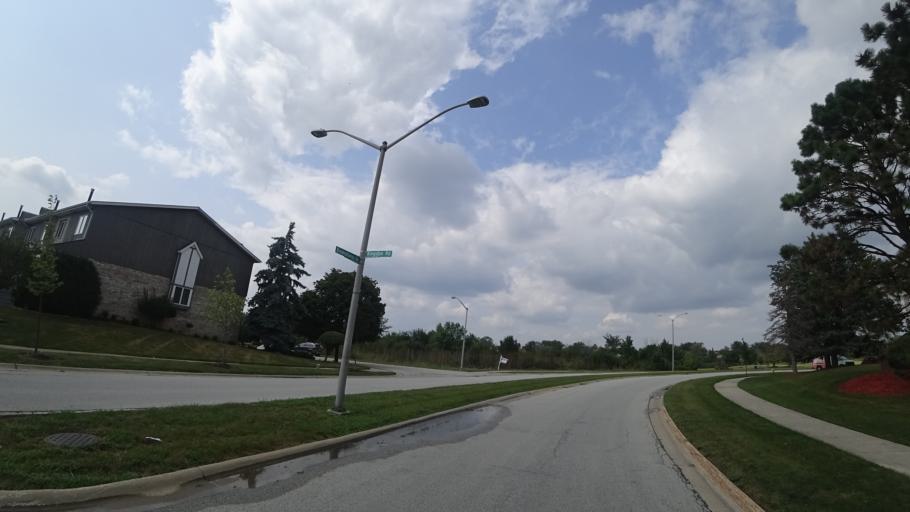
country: US
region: Illinois
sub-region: Cook County
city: Tinley Park
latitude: 41.5944
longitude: -87.7880
